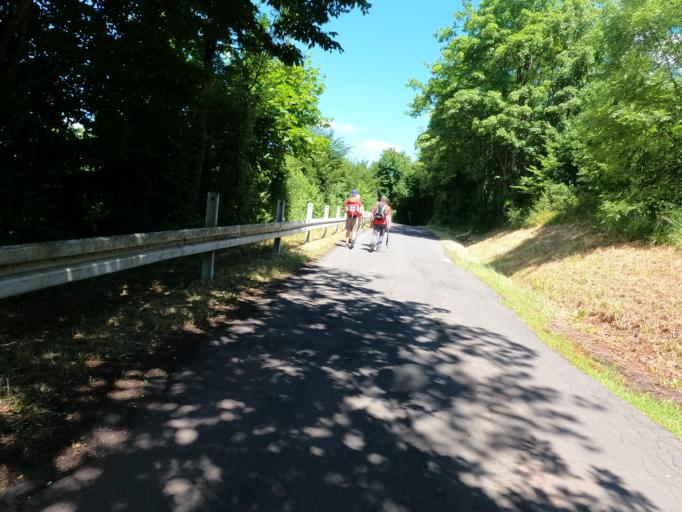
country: DE
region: Hesse
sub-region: Regierungsbezirk Darmstadt
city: Schluchtern
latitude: 50.3357
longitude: 9.6113
